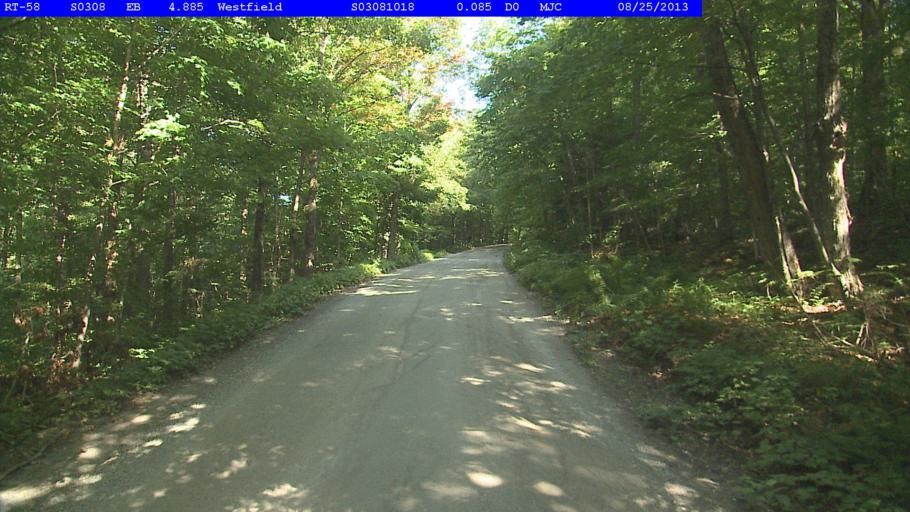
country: US
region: Vermont
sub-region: Franklin County
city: Richford
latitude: 44.8409
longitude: -72.5316
